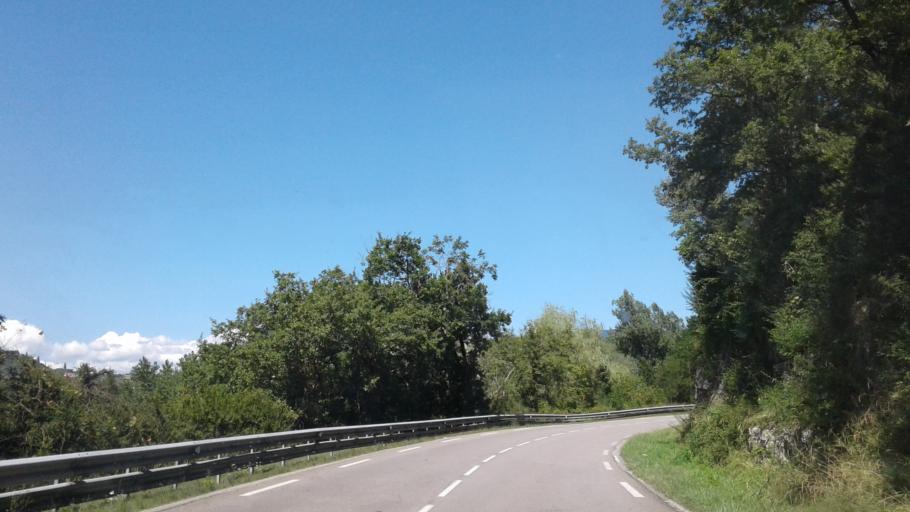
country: FR
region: Rhone-Alpes
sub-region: Departement de l'Ain
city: Virieu-le-Grand
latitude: 45.8624
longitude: 5.6675
